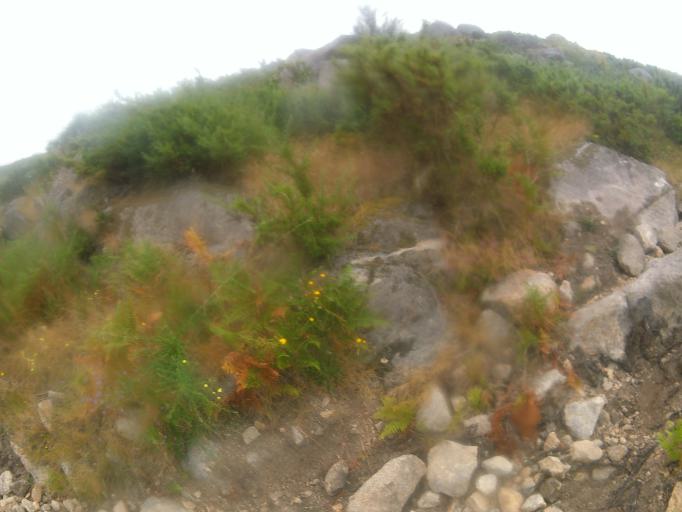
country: PT
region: Viana do Castelo
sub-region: Ponte de Lima
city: Ponte de Lima
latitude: 41.7139
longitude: -8.6015
